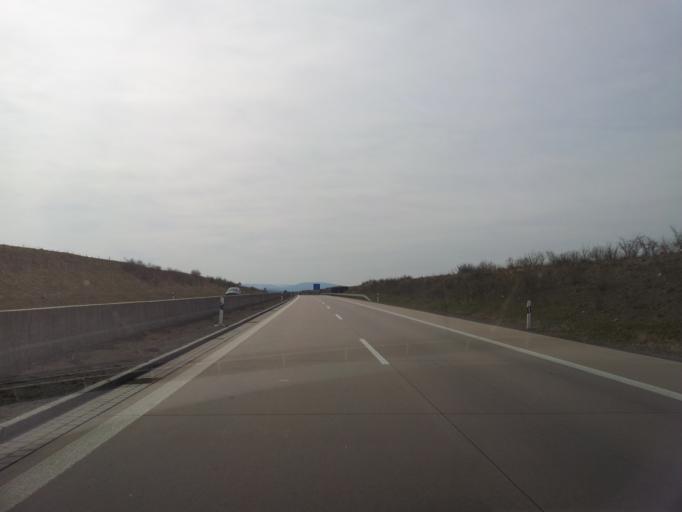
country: DE
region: Bavaria
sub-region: Regierungsbezirk Unterfranken
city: Hendungen
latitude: 50.4271
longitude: 10.3706
